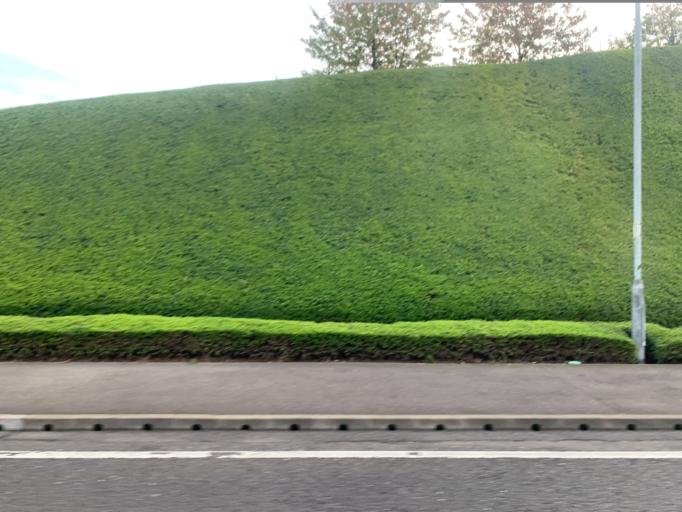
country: GB
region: England
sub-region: Buckinghamshire
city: Iver
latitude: 51.4755
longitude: -0.4949
